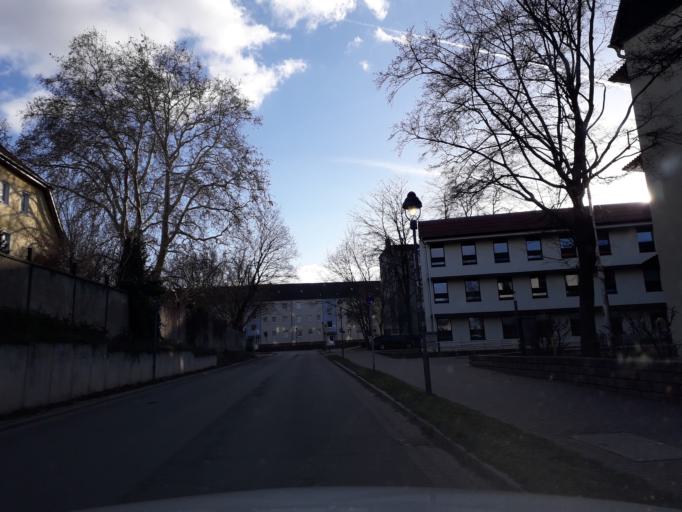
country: DE
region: Brandenburg
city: Nauen
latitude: 52.6055
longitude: 12.8847
